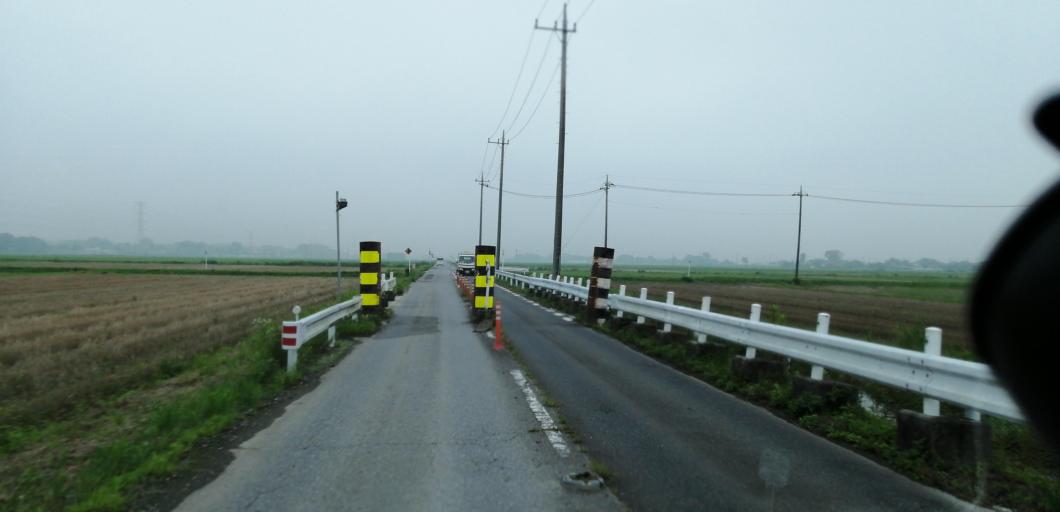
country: JP
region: Chiba
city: Noda
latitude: 35.9849
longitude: 139.8790
